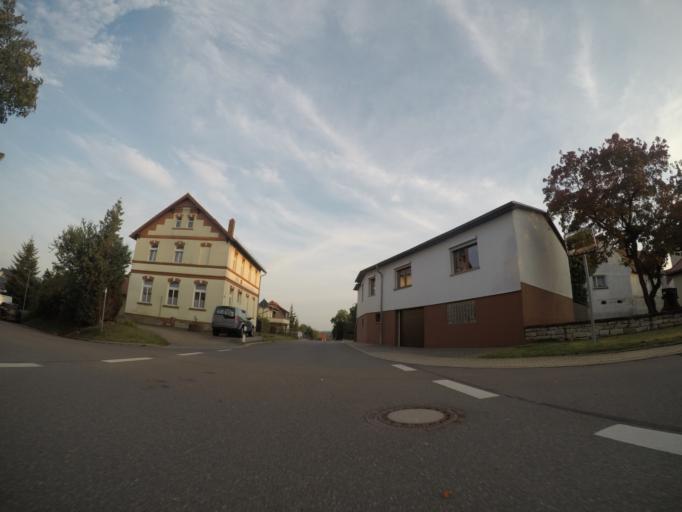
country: DE
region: Thuringia
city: Wildenborten
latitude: 50.9109
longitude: 12.2846
